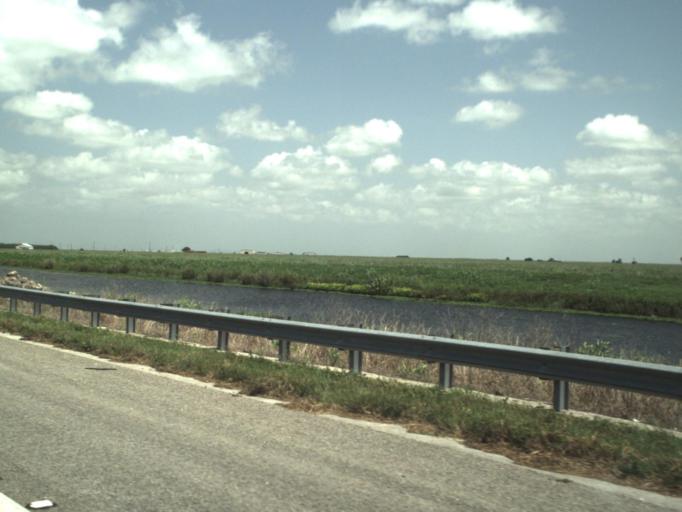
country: US
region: Florida
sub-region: Palm Beach County
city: Belle Glade Camp
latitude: 26.5524
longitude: -80.7065
